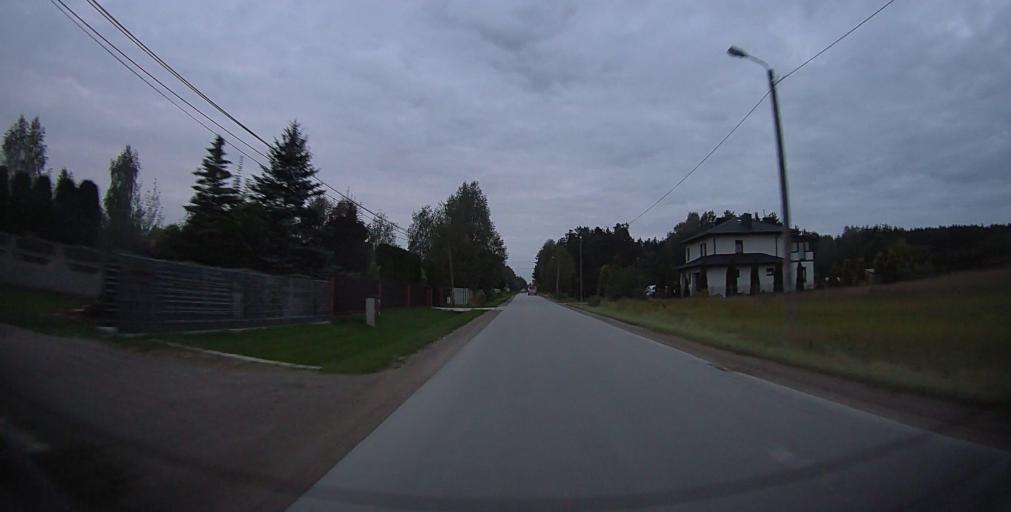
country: PL
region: Masovian Voivodeship
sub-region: Powiat radomski
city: Jedlinsk
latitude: 51.4670
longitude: 21.1296
